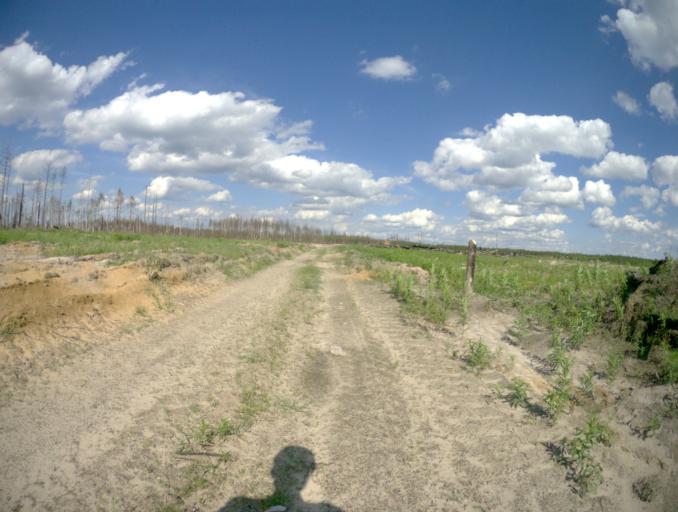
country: RU
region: Vladimir
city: Velikodvorskiy
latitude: 55.3104
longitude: 40.9152
